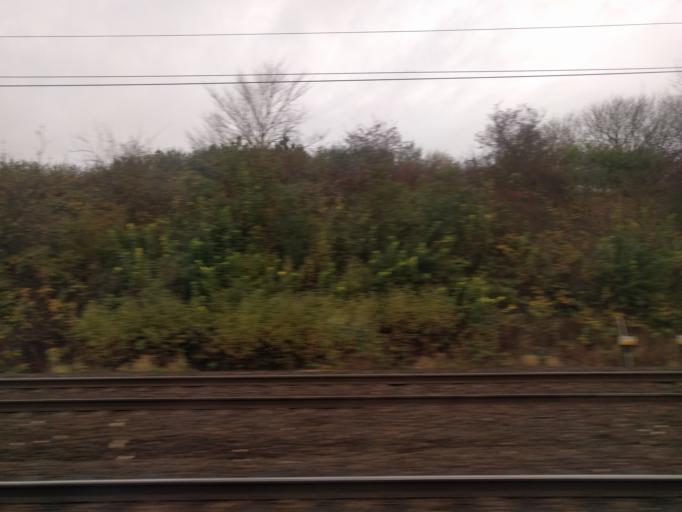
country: DK
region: Capital Region
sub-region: Hoje-Taastrup Kommune
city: Taastrup
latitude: 55.6471
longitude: 12.2540
